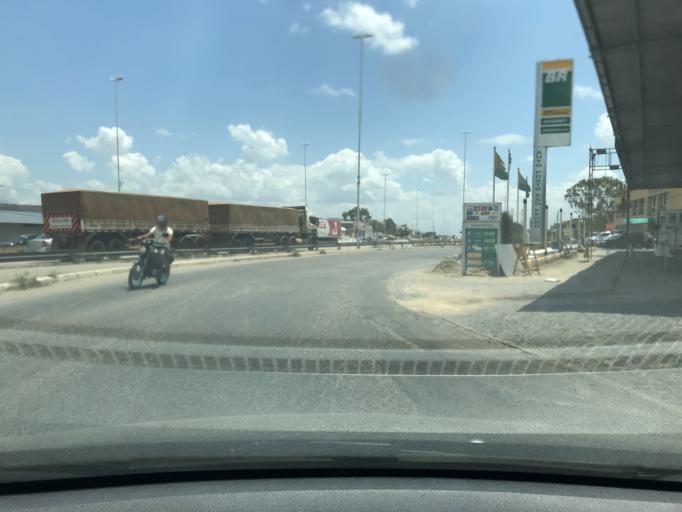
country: BR
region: Pernambuco
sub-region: Bezerros
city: Bezerros
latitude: -8.2382
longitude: -35.7454
